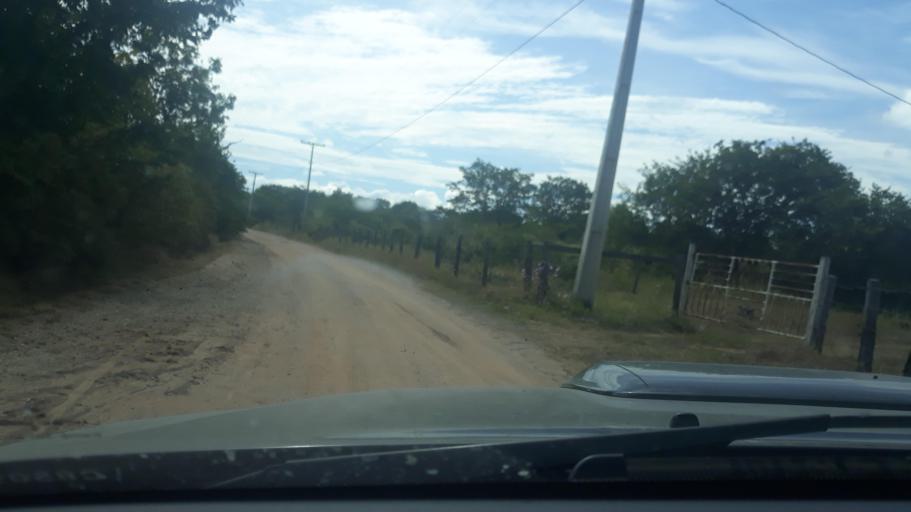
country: BR
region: Bahia
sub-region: Riacho De Santana
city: Riacho de Santana
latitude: -13.8869
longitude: -43.0232
